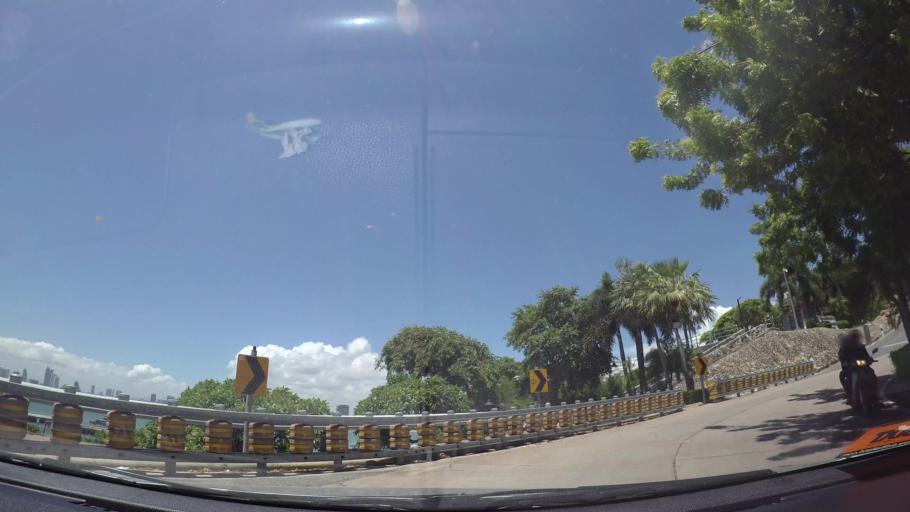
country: TH
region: Chon Buri
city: Phatthaya
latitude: 12.9280
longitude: 100.8630
